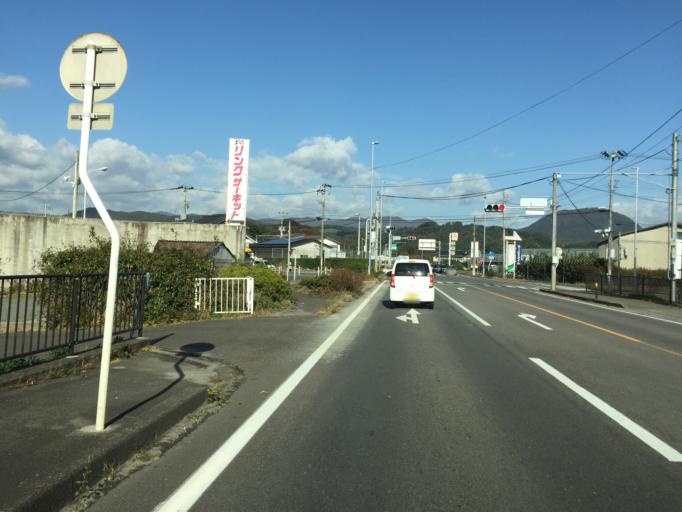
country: JP
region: Fukushima
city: Fukushima-shi
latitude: 37.8177
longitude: 140.4367
